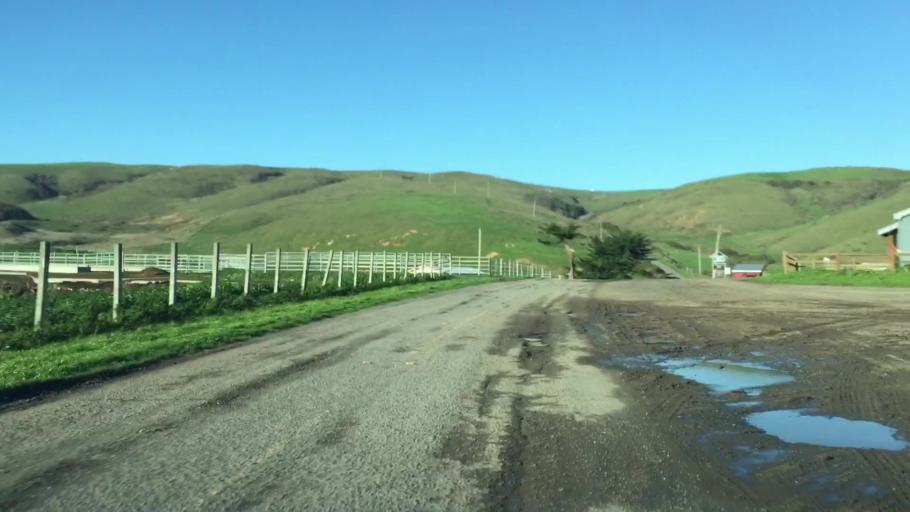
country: US
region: California
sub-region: Marin County
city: Inverness
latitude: 38.1594
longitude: -122.9383
